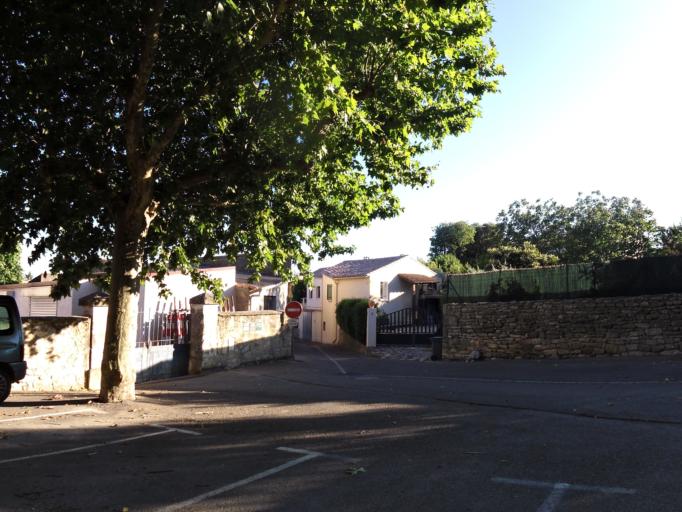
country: FR
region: Languedoc-Roussillon
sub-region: Departement du Gard
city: Villevieille
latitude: 43.7907
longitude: 4.1243
